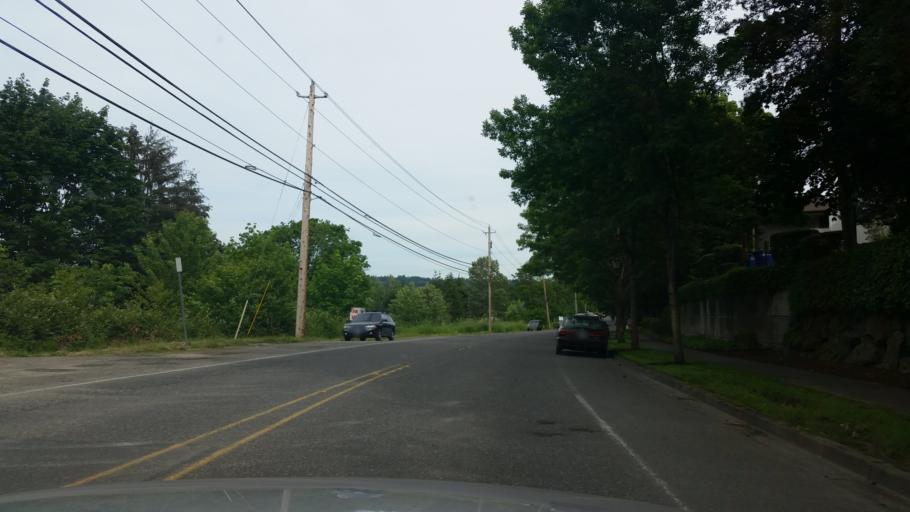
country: US
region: Washington
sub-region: King County
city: Woodinville
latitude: 47.7565
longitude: -122.1787
